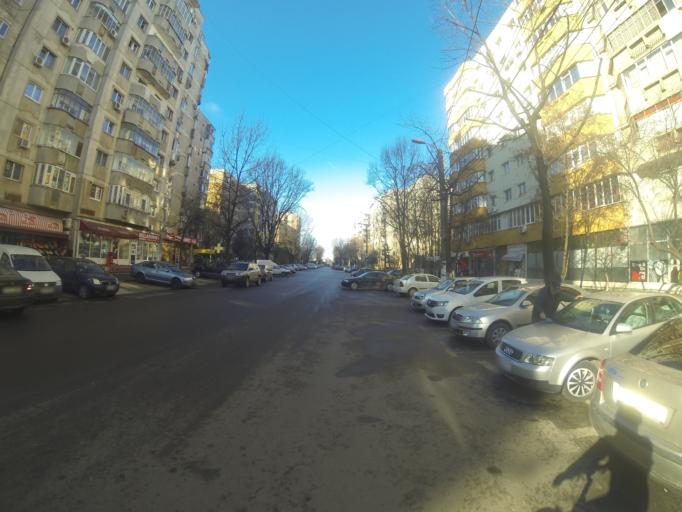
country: RO
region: Bucuresti
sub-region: Municipiul Bucuresti
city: Bucuresti
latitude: 44.4107
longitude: 26.0642
